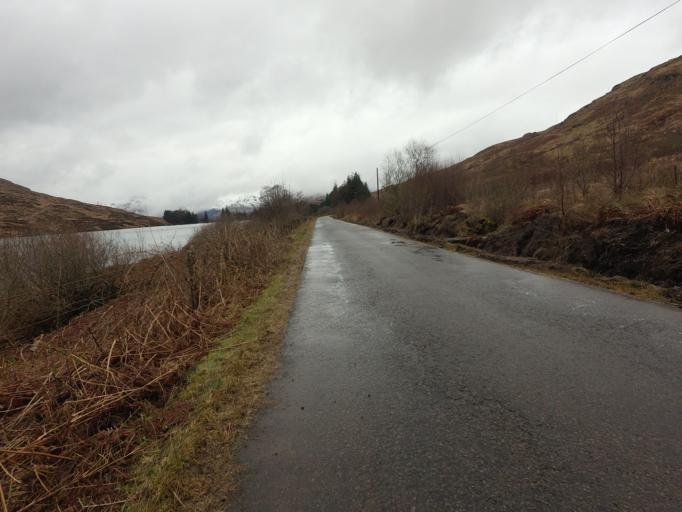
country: GB
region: Scotland
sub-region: Argyll and Bute
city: Garelochhead
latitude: 56.2486
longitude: -4.6406
